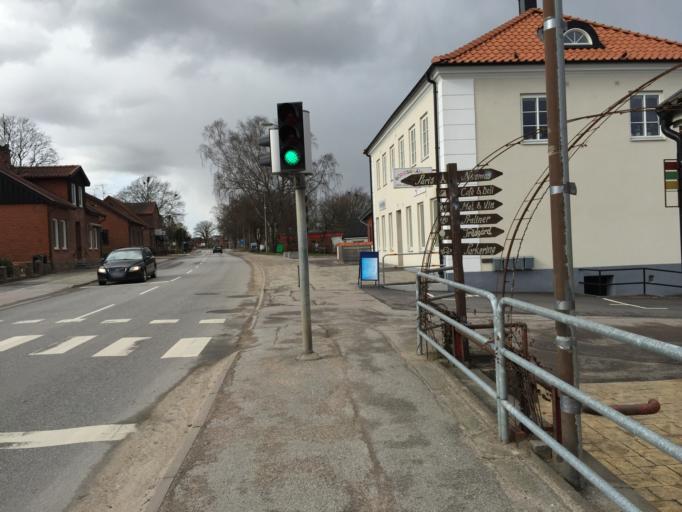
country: SE
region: Skane
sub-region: Lunds Kommun
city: Veberod
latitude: 55.6358
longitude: 13.4905
